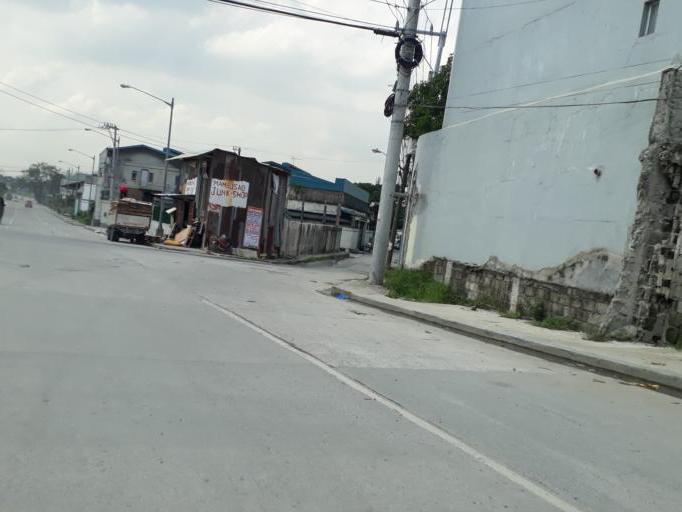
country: PH
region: Calabarzon
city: Bagong Pagasa
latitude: 14.7042
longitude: 121.0140
